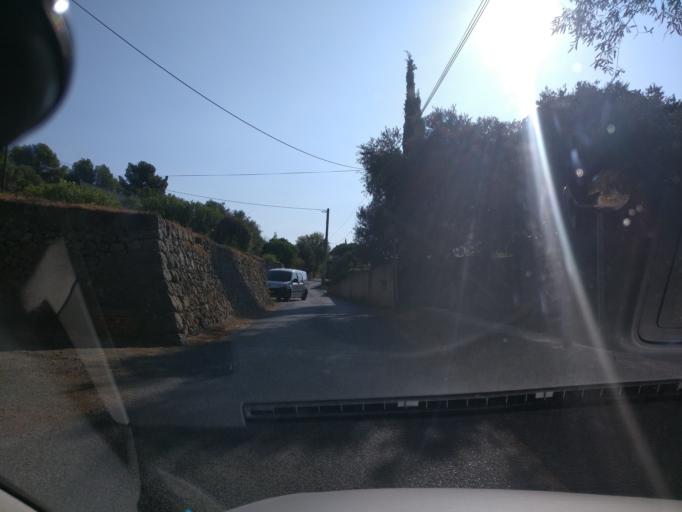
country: FR
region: Provence-Alpes-Cote d'Azur
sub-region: Departement du Var
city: Ollioules
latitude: 43.1341
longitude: 5.8338
